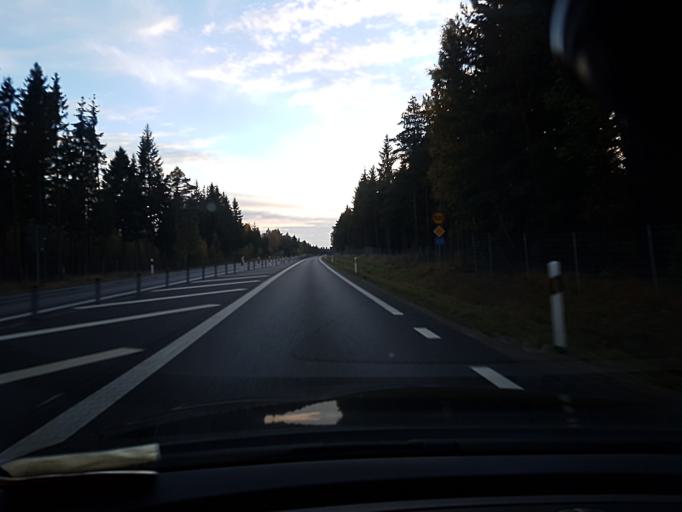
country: SE
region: Kronoberg
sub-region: Ljungby Kommun
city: Ljungby
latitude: 56.7727
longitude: 13.8081
